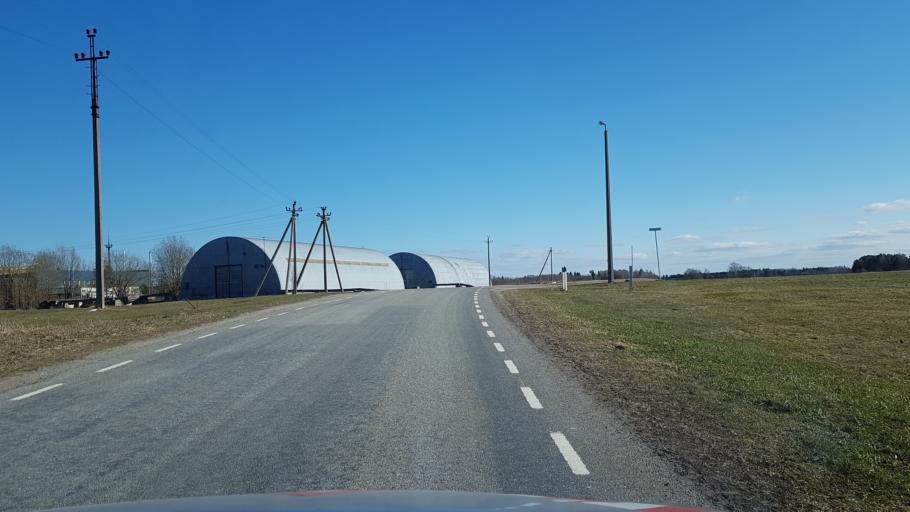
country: EE
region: Laeaene-Virumaa
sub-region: Kadrina vald
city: Kadrina
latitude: 59.3730
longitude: 26.0445
